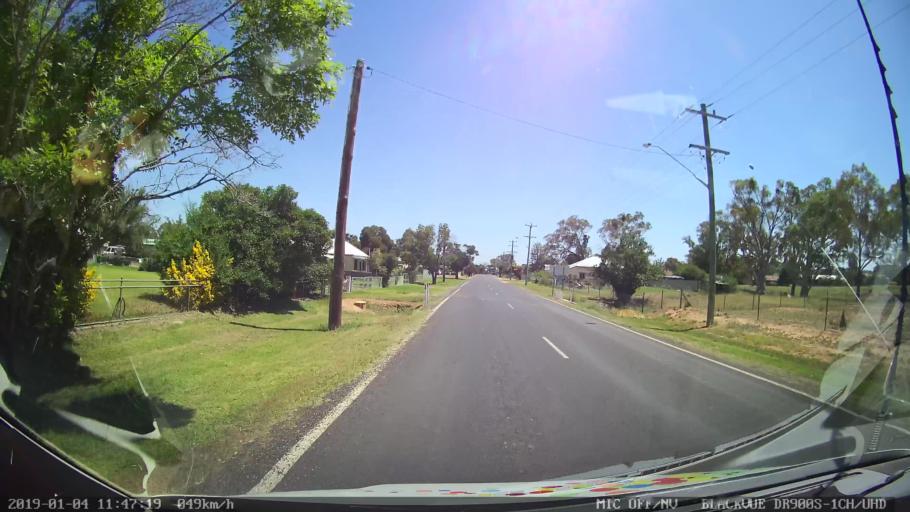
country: AU
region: New South Wales
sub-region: Cabonne
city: Molong
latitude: -32.9338
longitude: 148.7551
